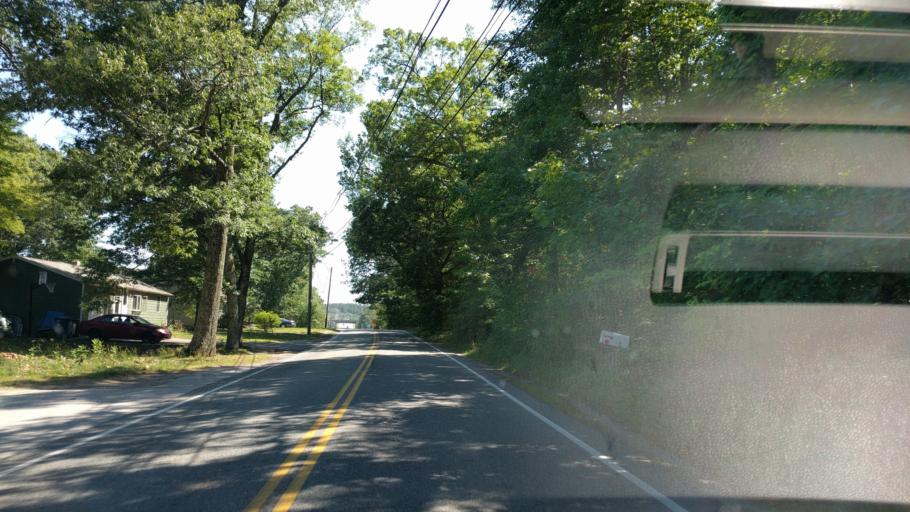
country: US
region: Massachusetts
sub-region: Worcester County
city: East Douglas
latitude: 42.0946
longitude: -71.6939
